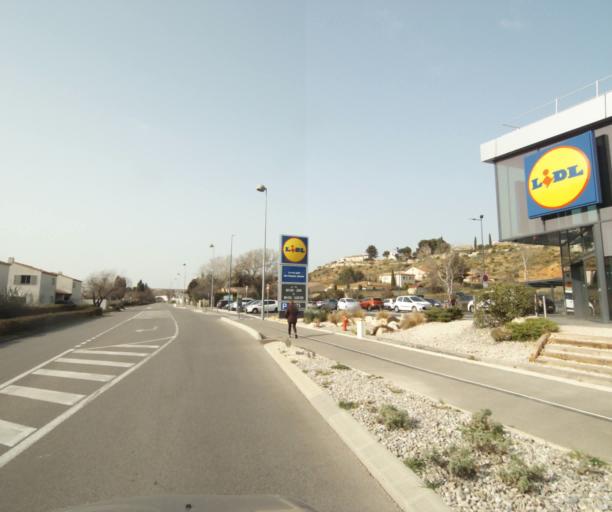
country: FR
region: Provence-Alpes-Cote d'Azur
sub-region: Departement des Bouches-du-Rhone
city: Les Pennes-Mirabeau
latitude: 43.4230
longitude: 5.2853
